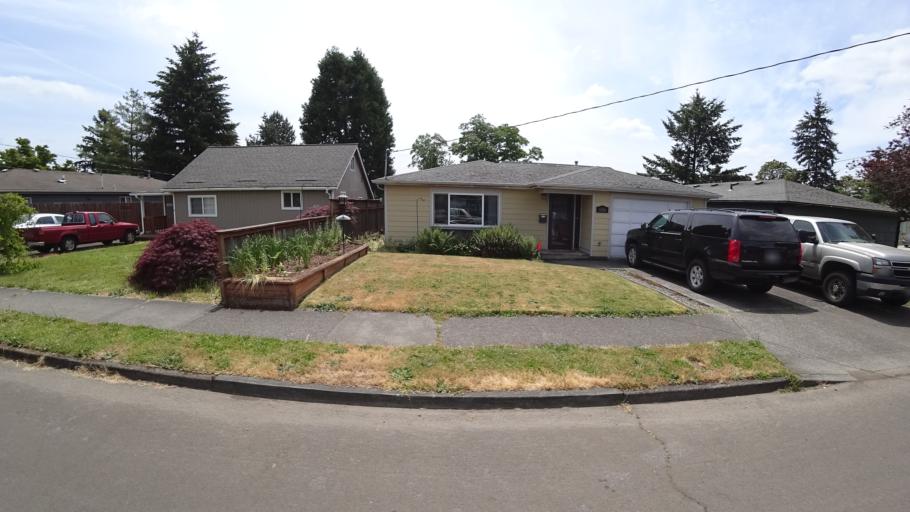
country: US
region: Oregon
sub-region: Multnomah County
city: Lents
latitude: 45.4641
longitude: -122.5920
